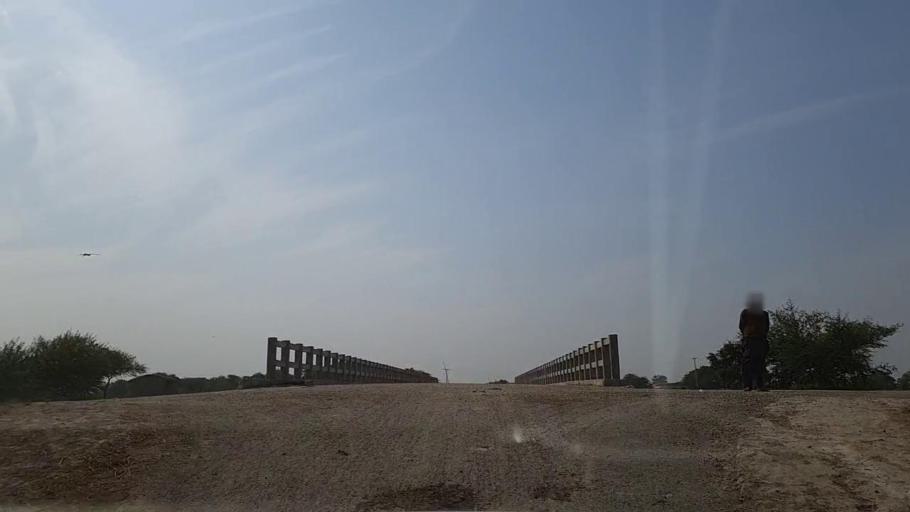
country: PK
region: Sindh
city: Mirpur Batoro
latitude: 24.6399
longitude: 68.2242
